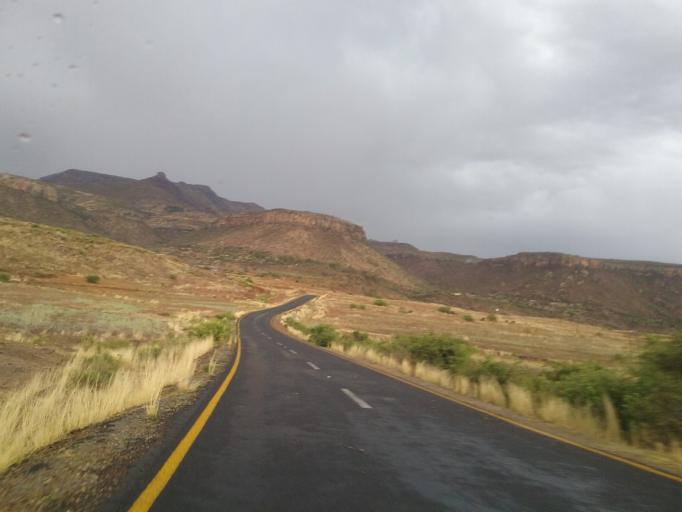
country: LS
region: Quthing
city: Quthing
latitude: -30.3200
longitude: 27.7425
